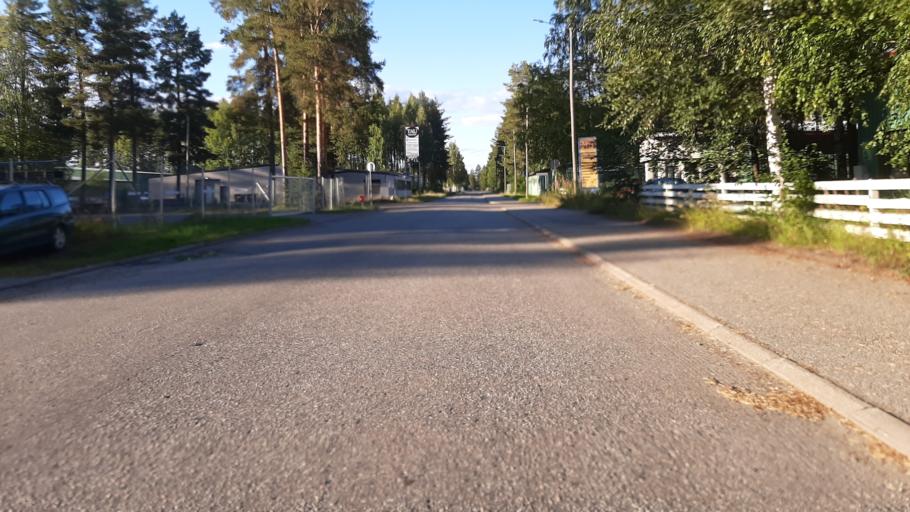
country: FI
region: North Karelia
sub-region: Joensuu
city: Joensuu
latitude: 62.6192
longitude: 29.7429
